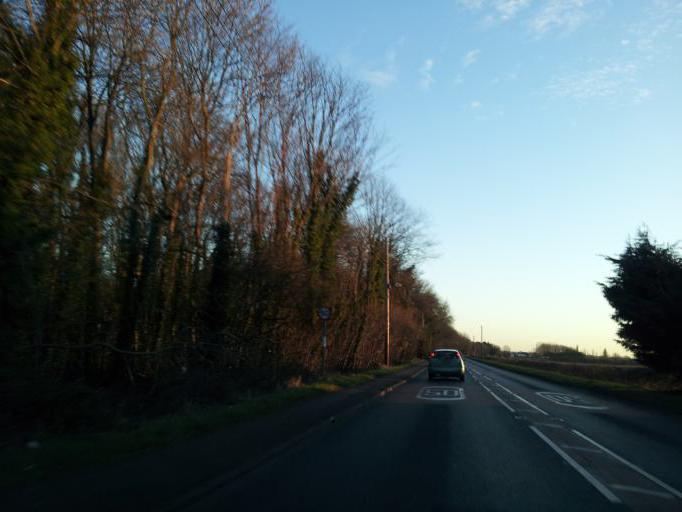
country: GB
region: England
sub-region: Lincolnshire
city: Sudbrooke
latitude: 53.2674
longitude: -0.4343
